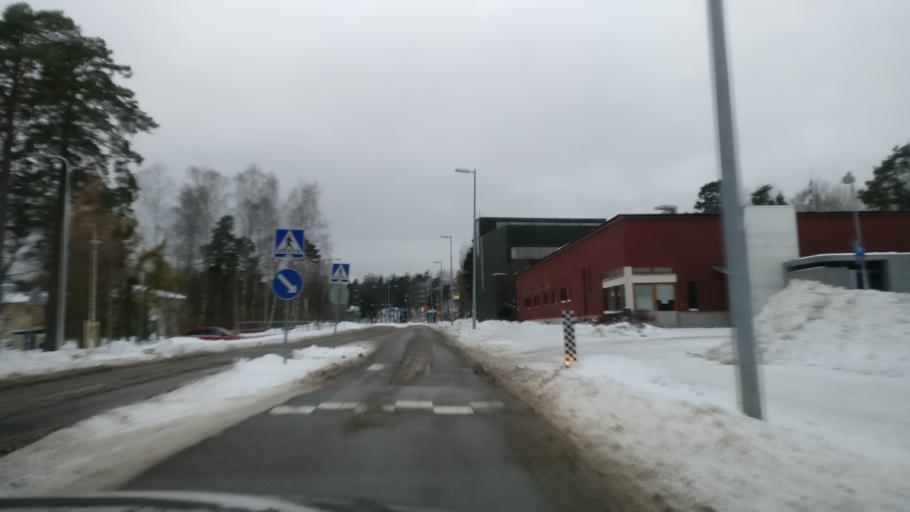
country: FI
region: Uusimaa
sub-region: Helsinki
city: Vantaa
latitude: 60.1782
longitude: 25.0550
